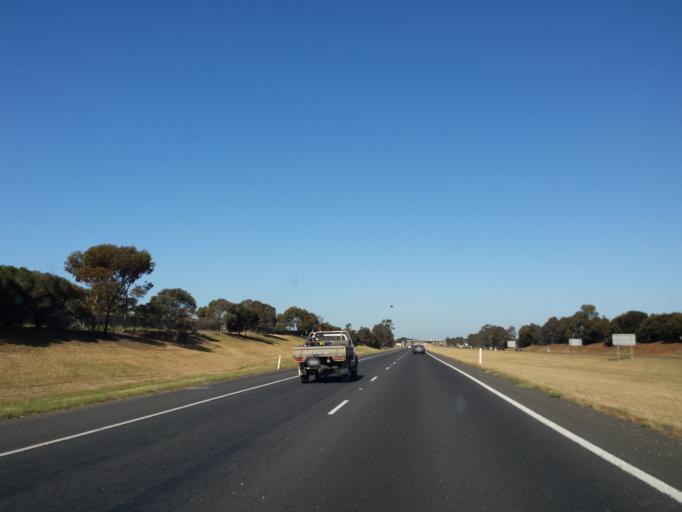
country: AU
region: Victoria
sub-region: Melton
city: Brookfield
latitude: -37.6886
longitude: 144.5528
